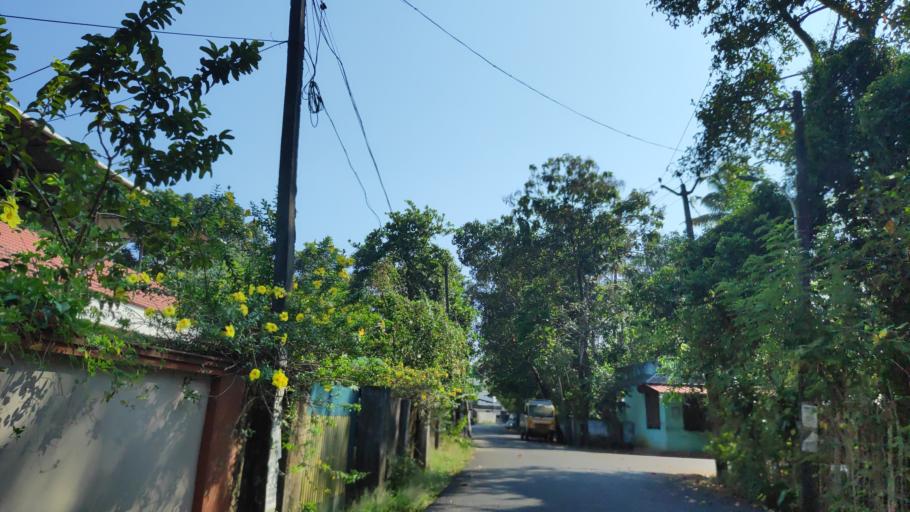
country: IN
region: Kerala
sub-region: Alappuzha
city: Alleppey
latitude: 9.5481
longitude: 76.3199
